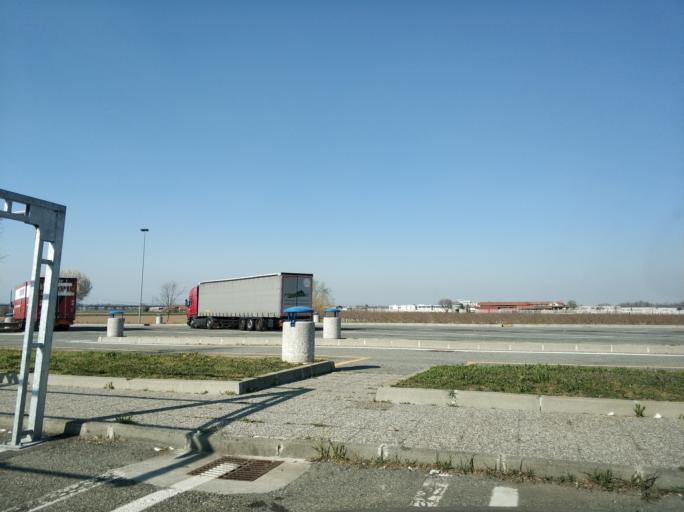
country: IT
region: Piedmont
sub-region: Provincia di Vercelli
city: Santhia
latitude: 45.3677
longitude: 8.1445
